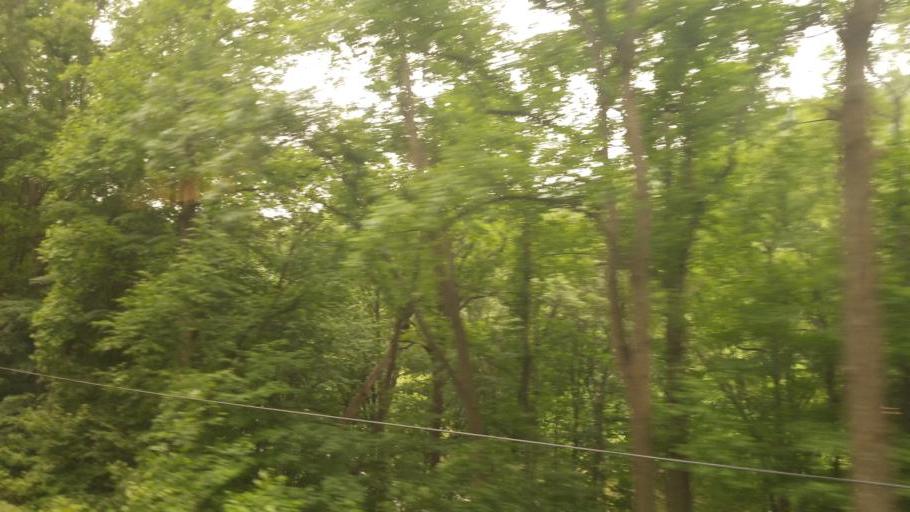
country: US
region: Pennsylvania
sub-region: Fayette County
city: South Connellsville
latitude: 39.9137
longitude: -79.4724
